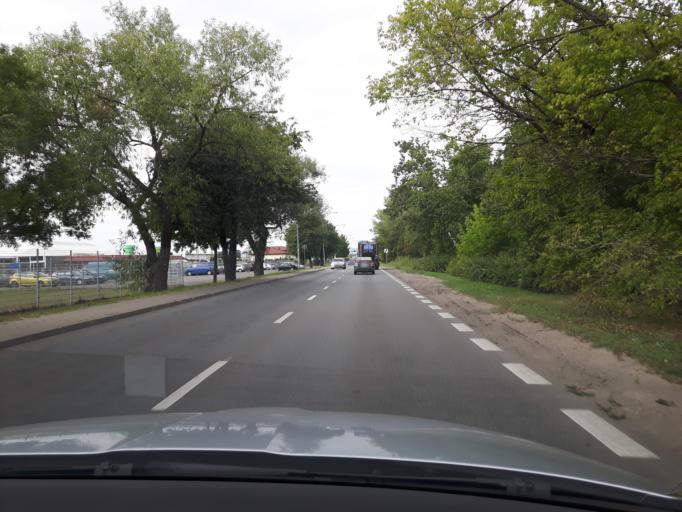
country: PL
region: Masovian Voivodeship
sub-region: Warszawa
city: Targowek
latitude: 52.3315
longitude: 21.0305
